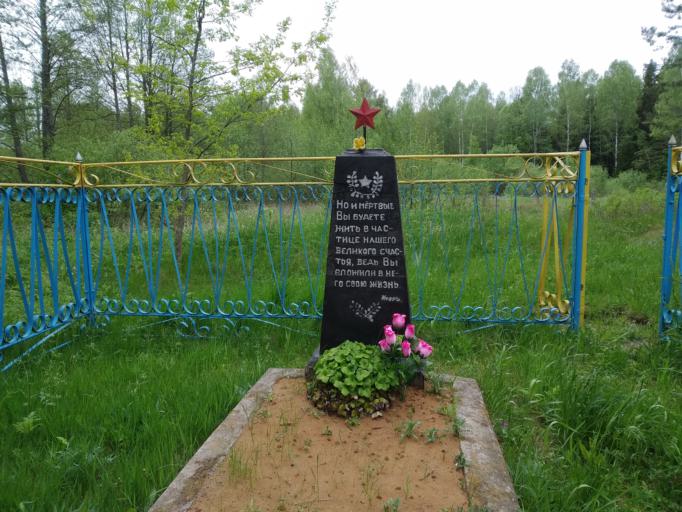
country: BY
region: Grodnenskaya
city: Mir
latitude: 53.6500
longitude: 26.3950
